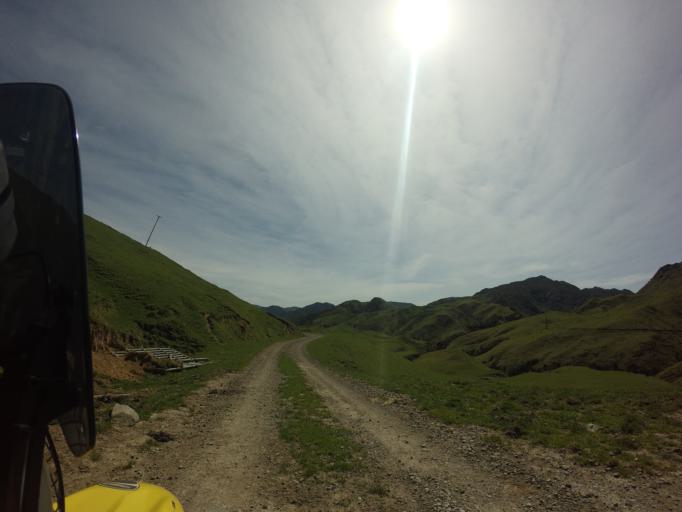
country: NZ
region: Bay of Plenty
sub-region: Opotiki District
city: Opotiki
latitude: -38.4571
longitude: 177.3742
